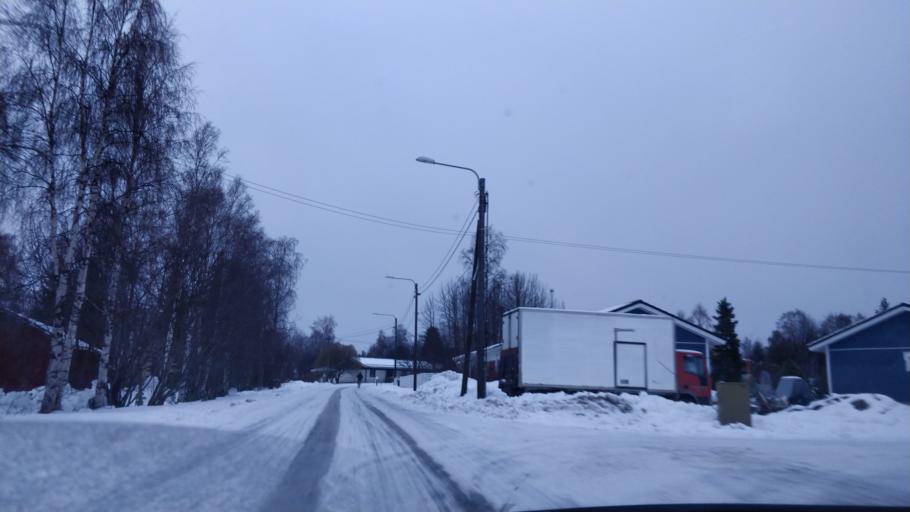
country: FI
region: Lapland
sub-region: Kemi-Tornio
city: Kemi
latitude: 65.7441
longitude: 24.5757
